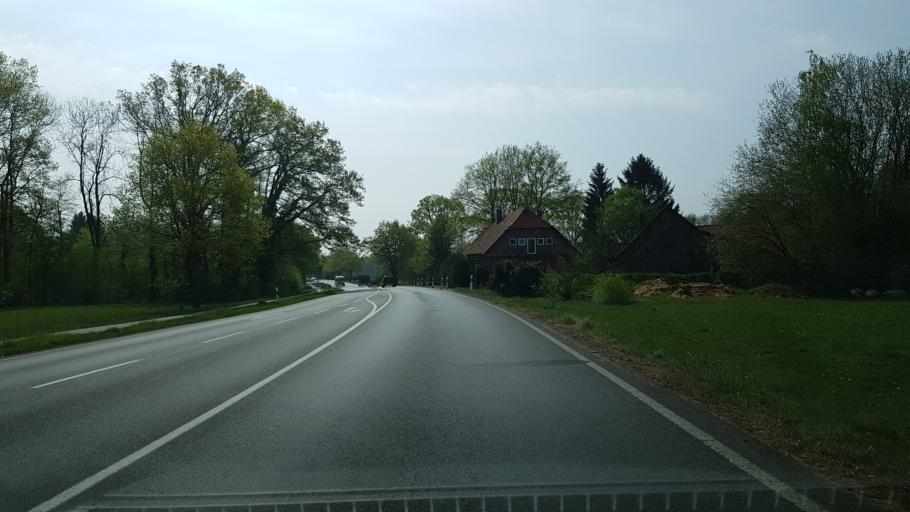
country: DE
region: Lower Saxony
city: Soltau
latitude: 52.9688
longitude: 9.8525
